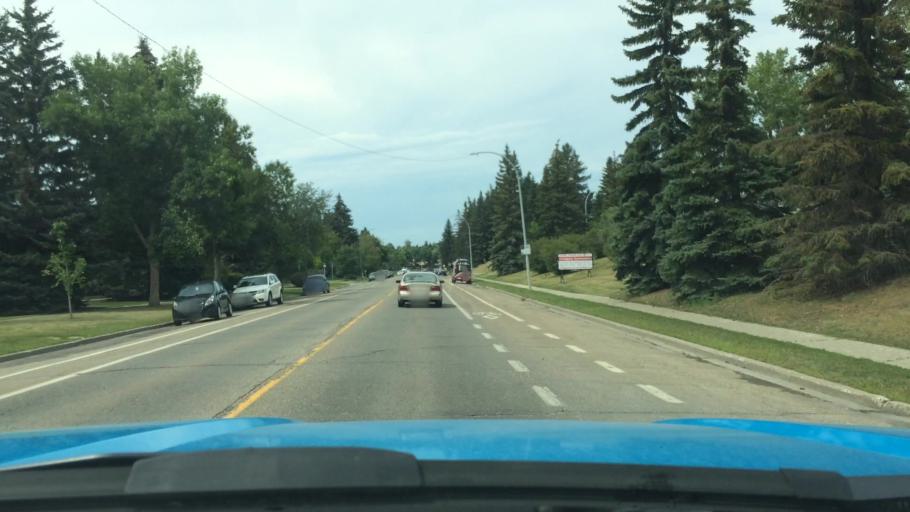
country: CA
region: Alberta
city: Calgary
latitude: 51.0796
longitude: -114.0872
